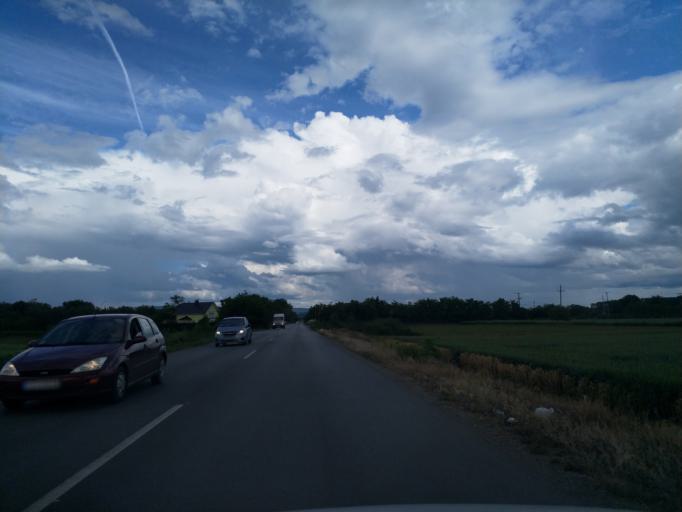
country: RS
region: Central Serbia
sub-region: Pomoravski Okrug
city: Cuprija
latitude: 43.9447
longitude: 21.3434
